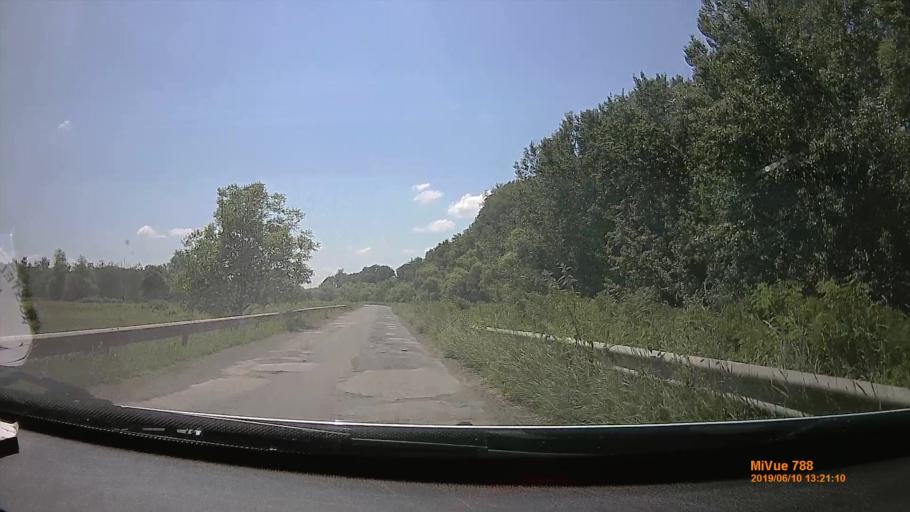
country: HU
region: Borsod-Abauj-Zemplen
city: Tiszaluc
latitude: 48.0375
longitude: 21.0779
